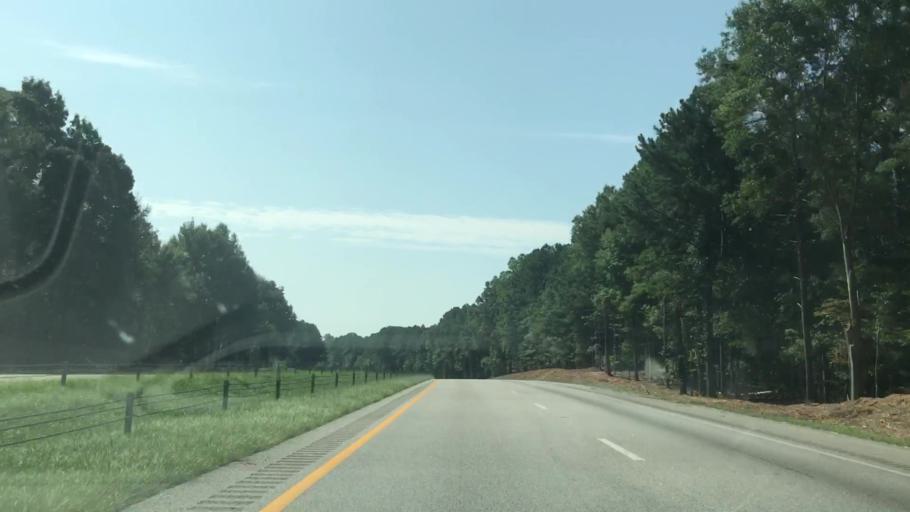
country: US
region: South Carolina
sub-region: Laurens County
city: Clinton
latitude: 34.5321
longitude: -81.8827
